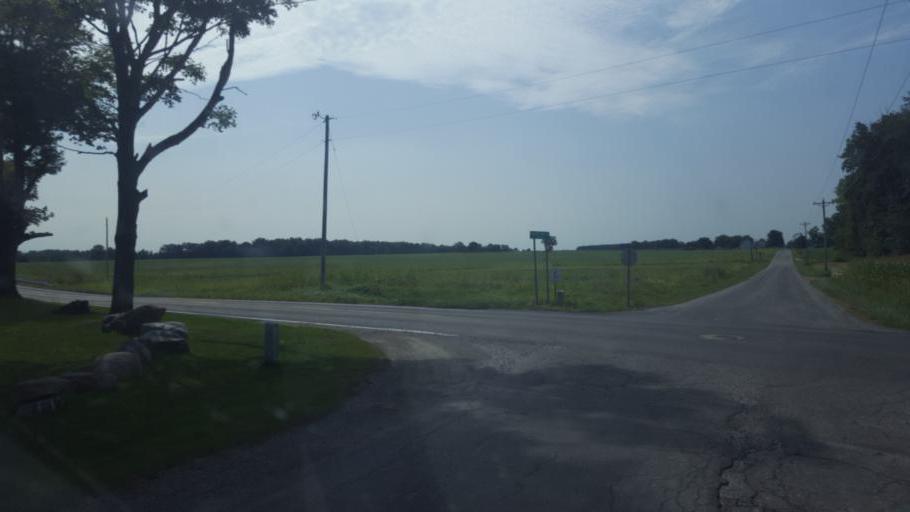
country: US
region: Ohio
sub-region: Morrow County
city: Cardington
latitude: 40.5365
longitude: -82.9956
